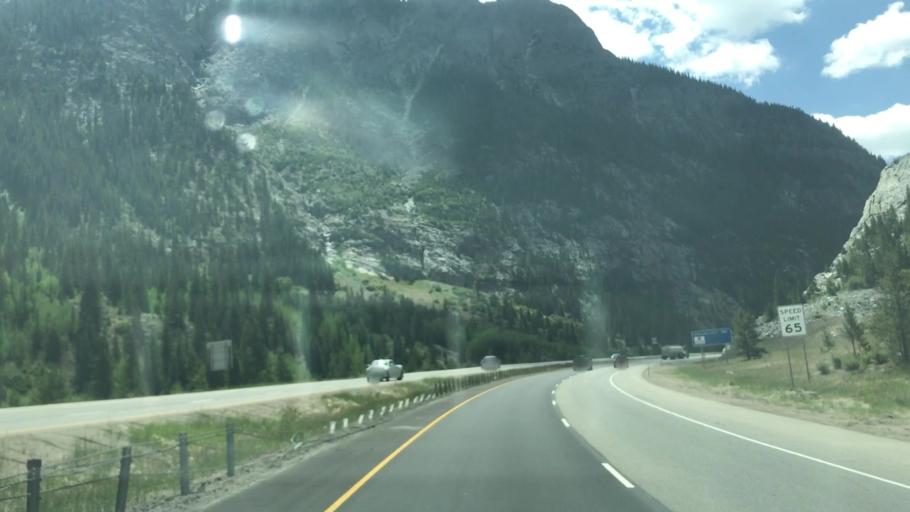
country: US
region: Colorado
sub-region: Summit County
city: Frisco
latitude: 39.5297
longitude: -106.1385
